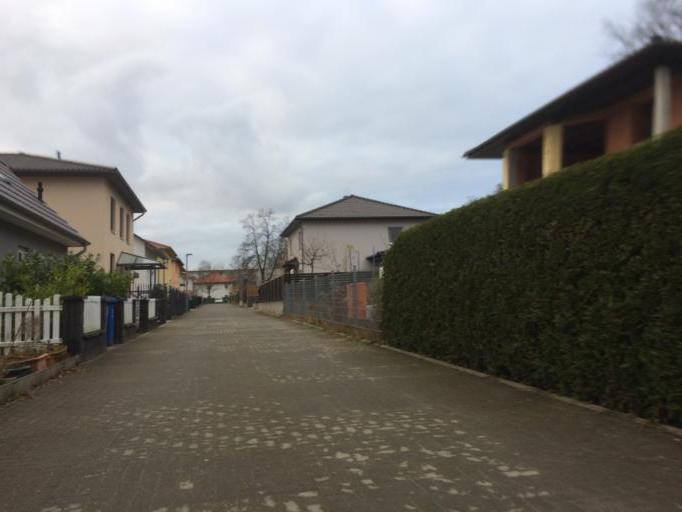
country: DE
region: Berlin
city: Lichtenberg
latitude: 52.5168
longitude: 13.5086
